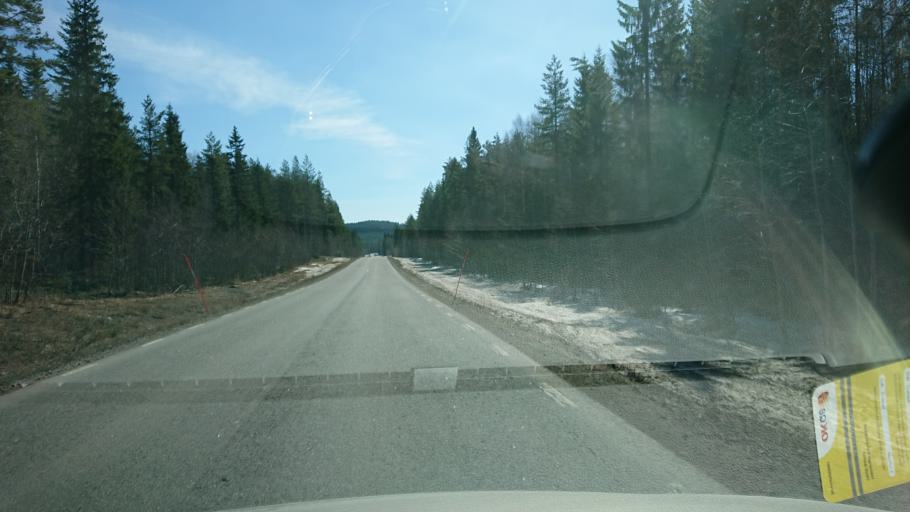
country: SE
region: Vaesternorrland
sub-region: Solleftea Kommun
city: As
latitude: 63.5771
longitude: 16.4386
